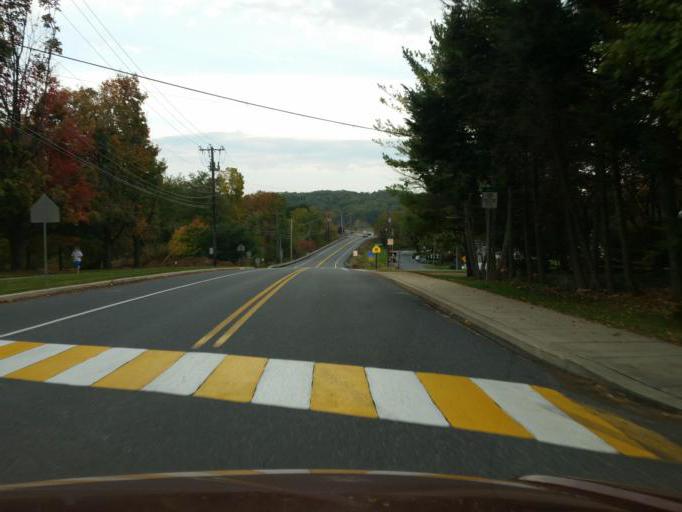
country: US
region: Pennsylvania
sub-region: Dauphin County
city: Hummelstown
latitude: 40.2622
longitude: -76.7020
